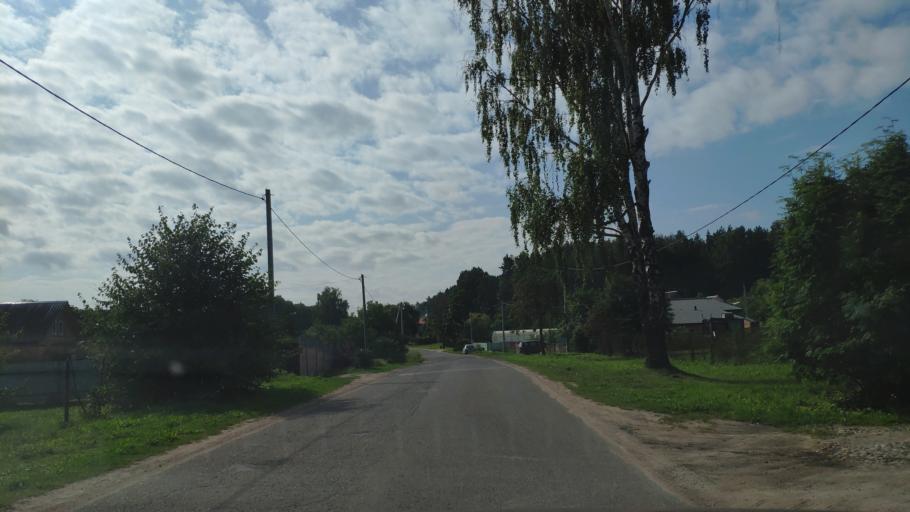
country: BY
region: Minsk
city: Zaslawye
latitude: 53.9910
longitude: 27.2851
